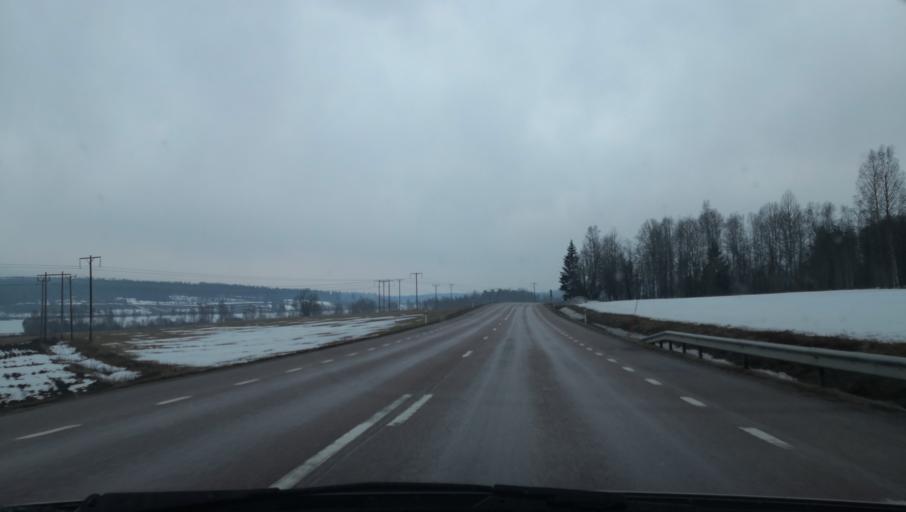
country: SE
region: Gaevleborg
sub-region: Nordanstigs Kommun
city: Bergsjoe
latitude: 62.0190
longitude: 17.2515
